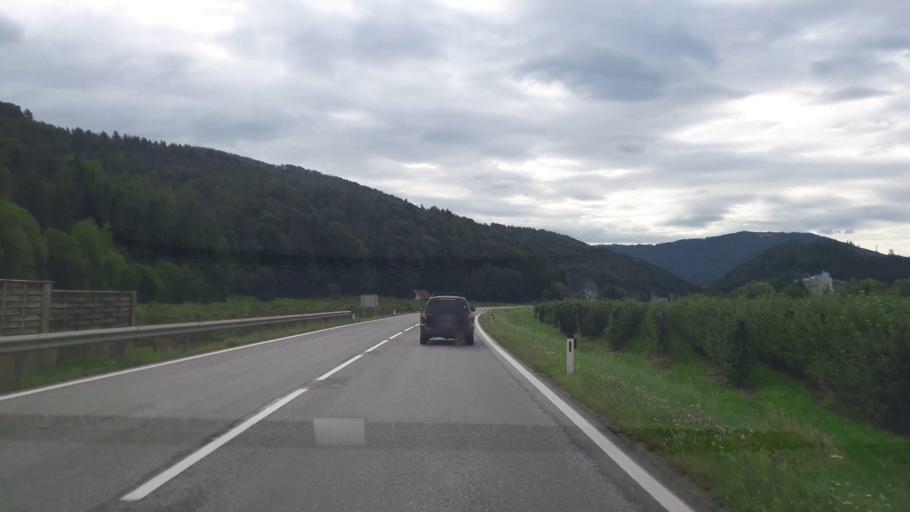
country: AT
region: Styria
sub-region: Politischer Bezirk Weiz
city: Anger
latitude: 47.2668
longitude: 15.7041
